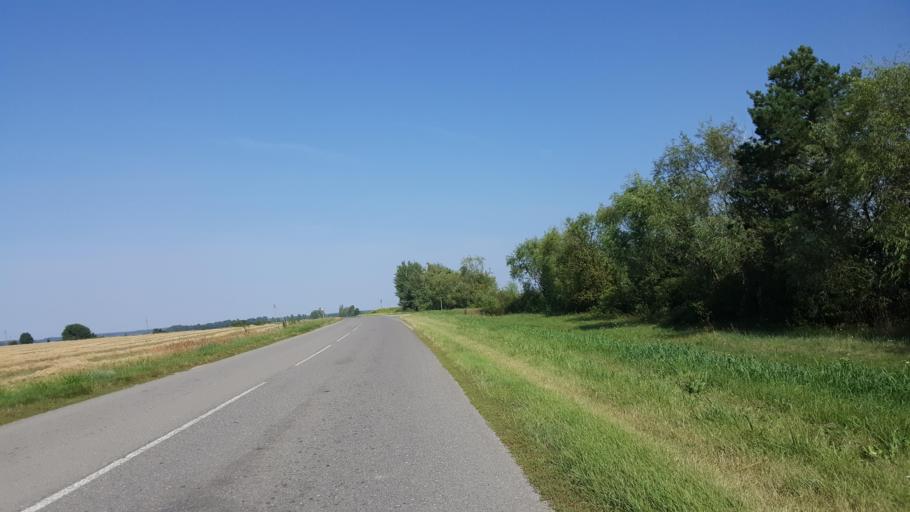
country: BY
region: Brest
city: Kamyanyets
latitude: 52.4749
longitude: 23.7065
